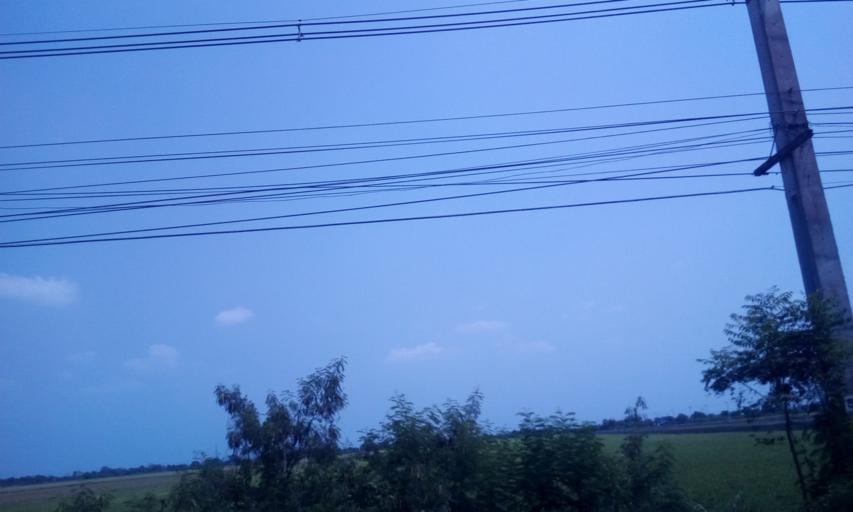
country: TH
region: Chachoengsao
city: Bang Nam Priao
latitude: 13.7787
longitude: 101.0624
